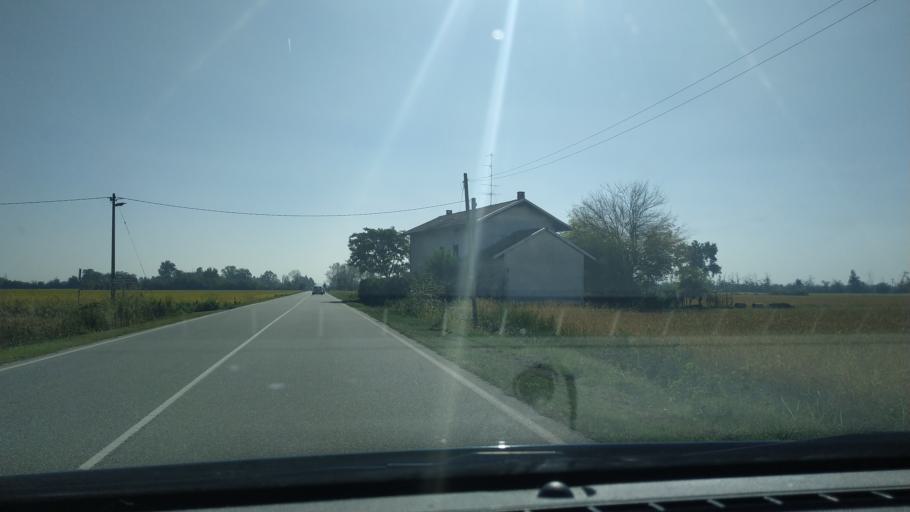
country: IT
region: Piedmont
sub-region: Provincia di Alessandria
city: Borgo San Martino
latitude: 45.1108
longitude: 8.5091
